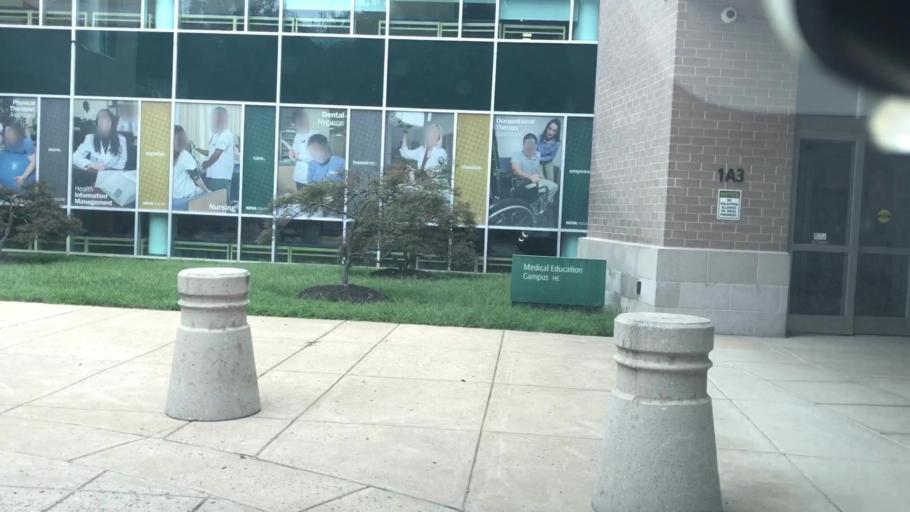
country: US
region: Virginia
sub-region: Fairfax County
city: Newington
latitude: 38.7628
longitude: -77.1772
